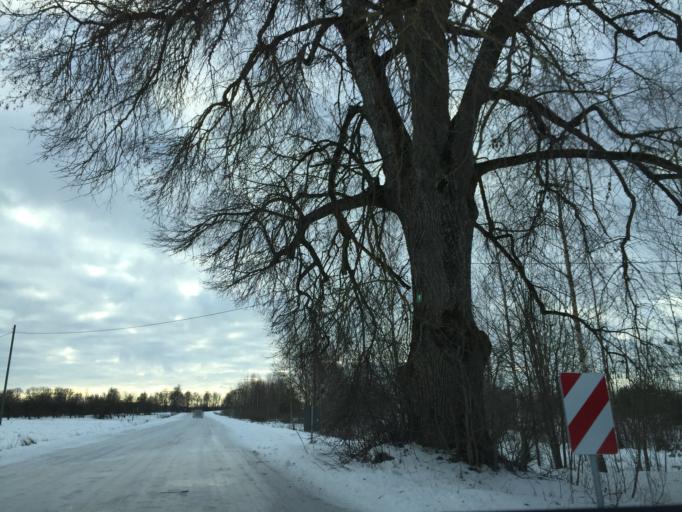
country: LV
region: Lielvarde
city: Lielvarde
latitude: 56.5716
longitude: 24.7340
